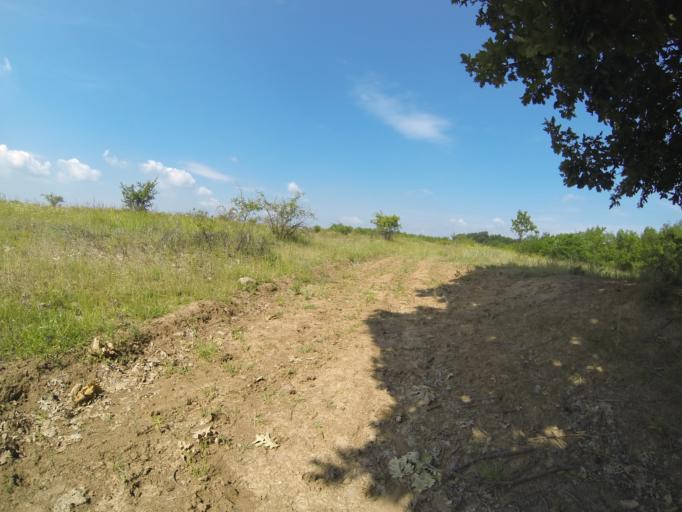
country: RO
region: Gorj
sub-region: Comuna Crusetu
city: Crusetu
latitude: 44.6106
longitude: 23.6521
